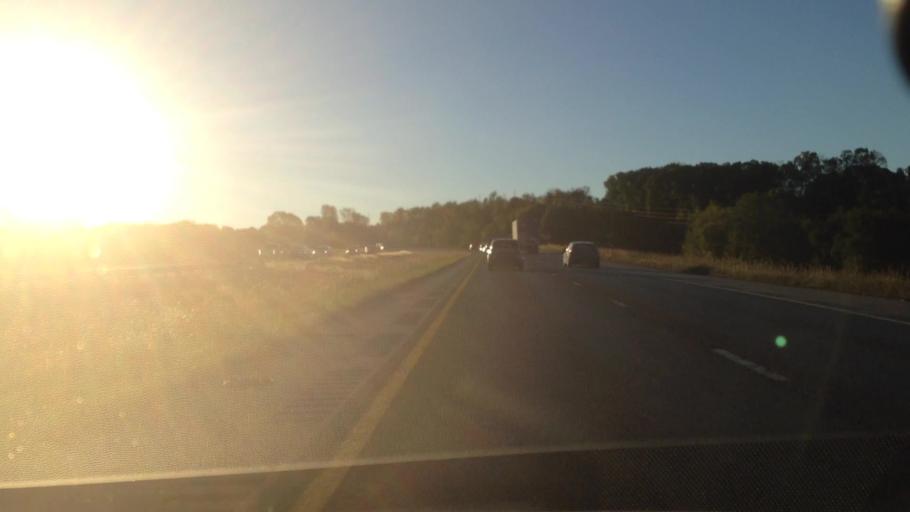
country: US
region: Kansas
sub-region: Johnson County
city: De Soto
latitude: 38.9502
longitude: -94.9050
